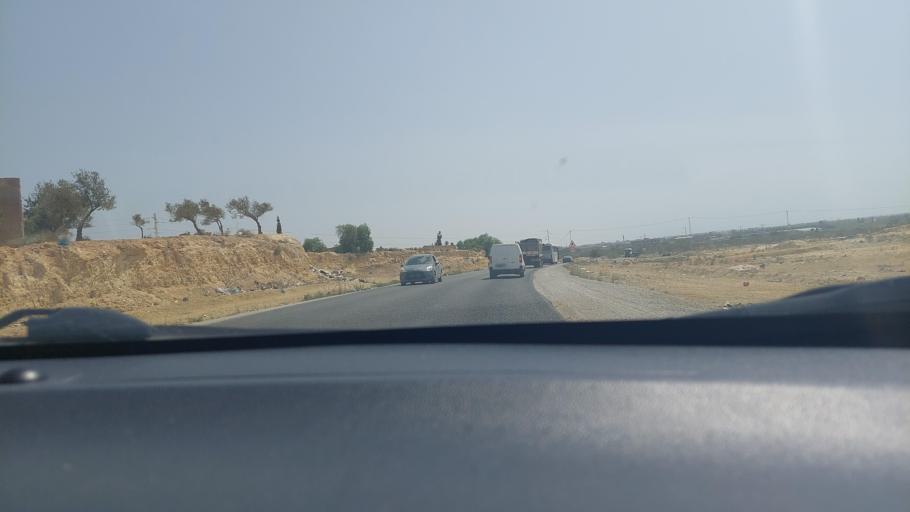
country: TN
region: Al Munastir
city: Qasr Hallal
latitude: 35.6367
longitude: 10.8693
